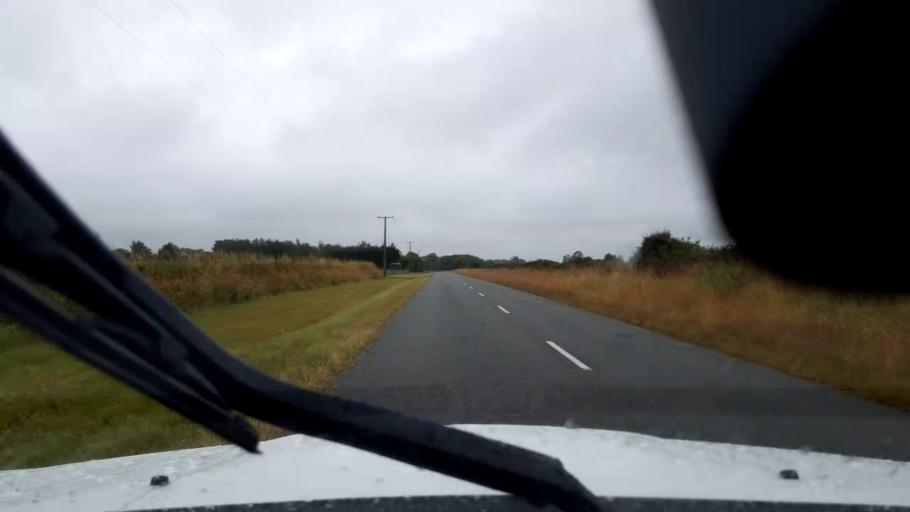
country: NZ
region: Canterbury
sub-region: Timaru District
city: Pleasant Point
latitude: -44.2535
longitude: 171.2485
